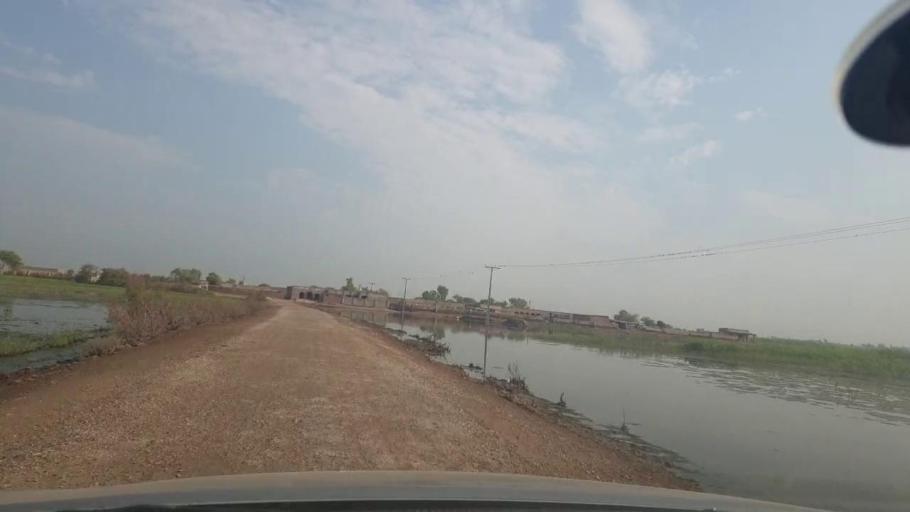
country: PK
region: Balochistan
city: Mehrabpur
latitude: 28.0719
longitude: 68.2110
